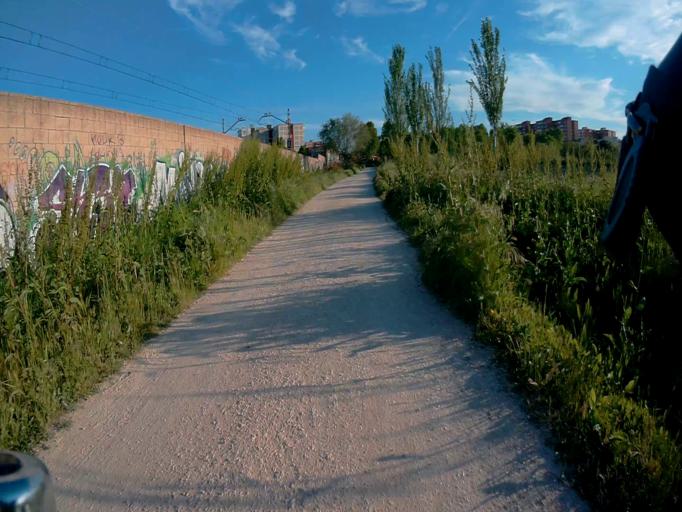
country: ES
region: Madrid
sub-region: Provincia de Madrid
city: Fuenlabrada
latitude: 40.2983
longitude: -3.7919
